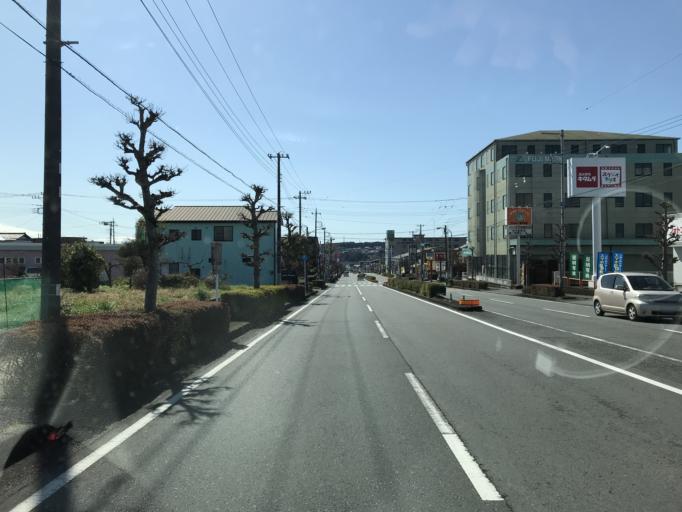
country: JP
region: Shizuoka
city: Fujinomiya
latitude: 35.2214
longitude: 138.6284
